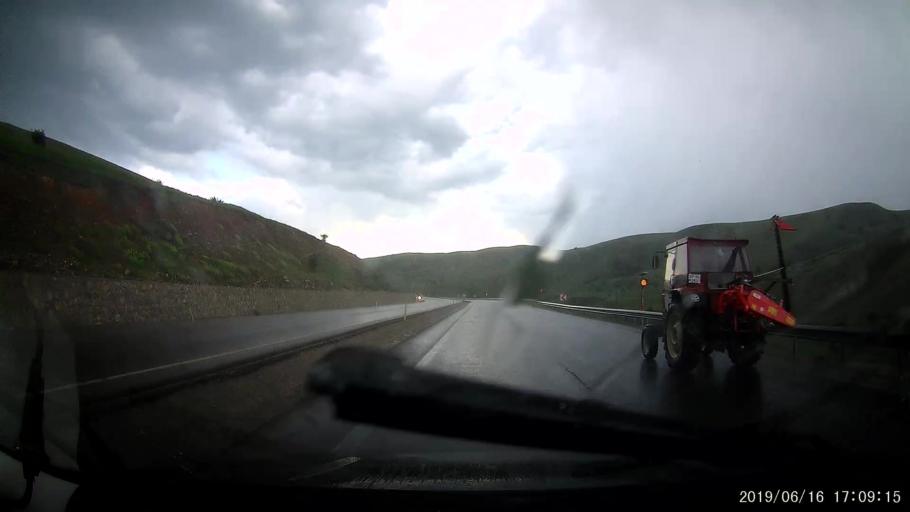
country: TR
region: Erzurum
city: Askale
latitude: 39.8977
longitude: 40.6514
